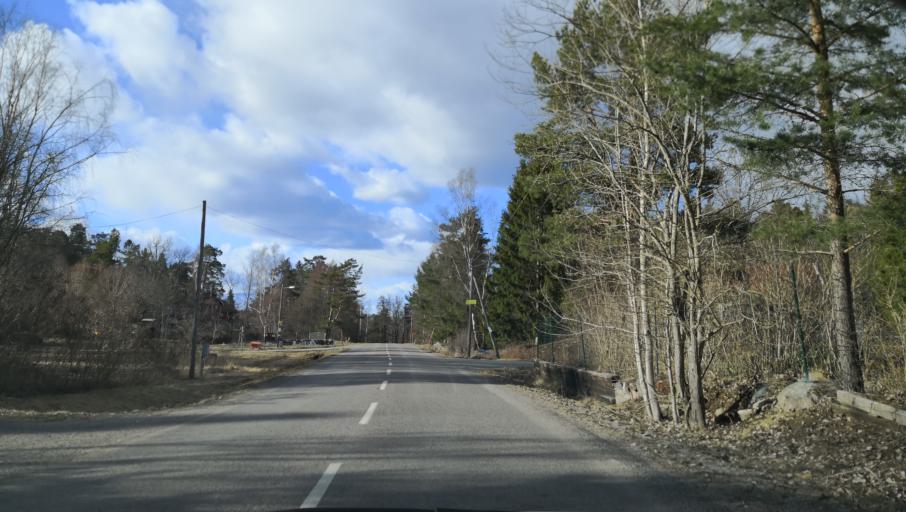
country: SE
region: Stockholm
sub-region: Varmdo Kommun
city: Hemmesta
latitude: 59.2829
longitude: 18.4942
